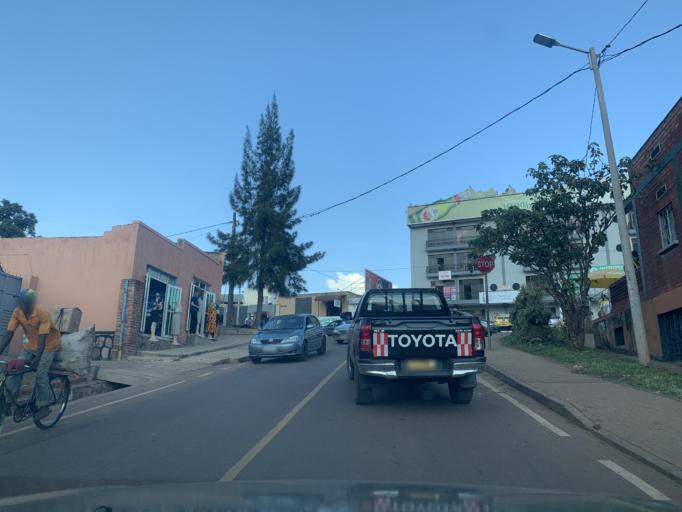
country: RW
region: Kigali
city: Kigali
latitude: -1.9663
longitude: 30.1021
